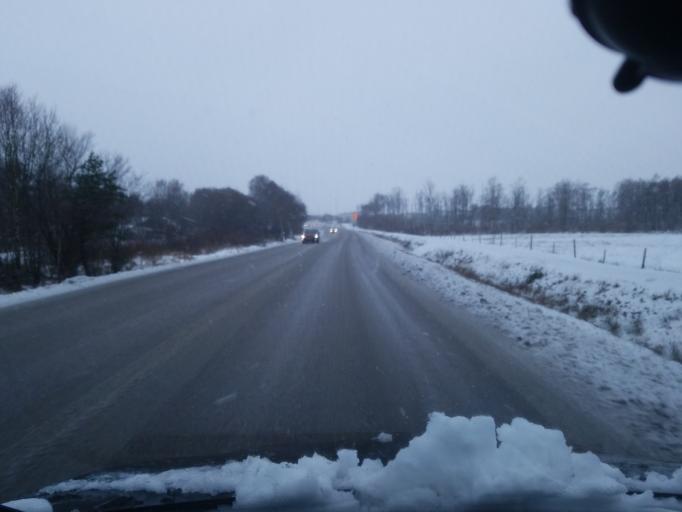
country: SE
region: Vaestra Goetaland
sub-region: Lysekils Kommun
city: Lysekil
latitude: 58.2937
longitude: 11.4700
